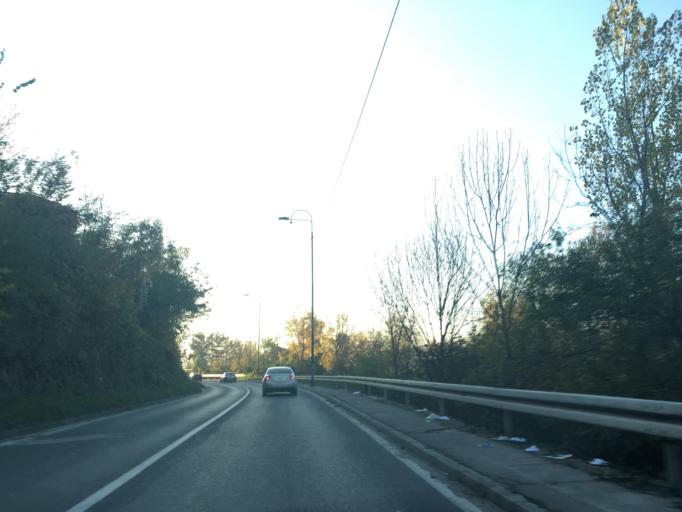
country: BA
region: Federation of Bosnia and Herzegovina
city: Kobilja Glava
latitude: 43.8530
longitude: 18.4201
